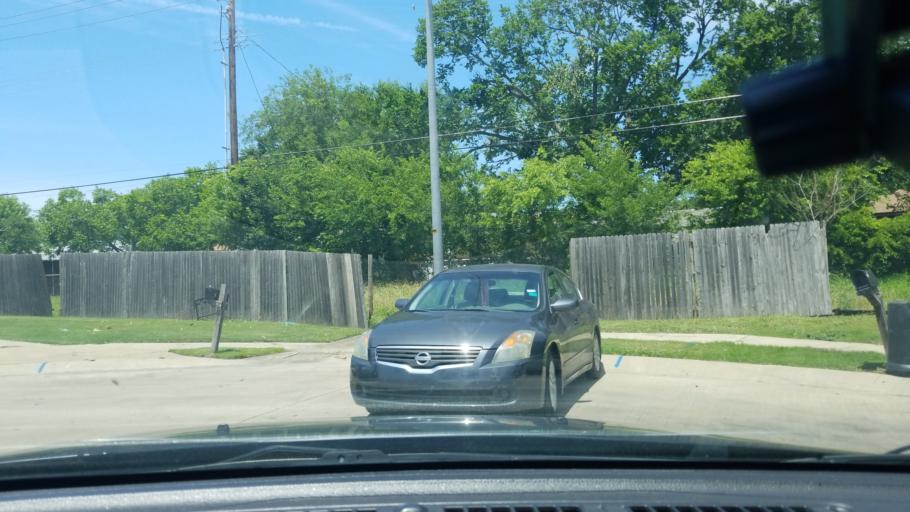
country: US
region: Texas
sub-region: Dallas County
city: Mesquite
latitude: 32.7832
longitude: -96.6185
